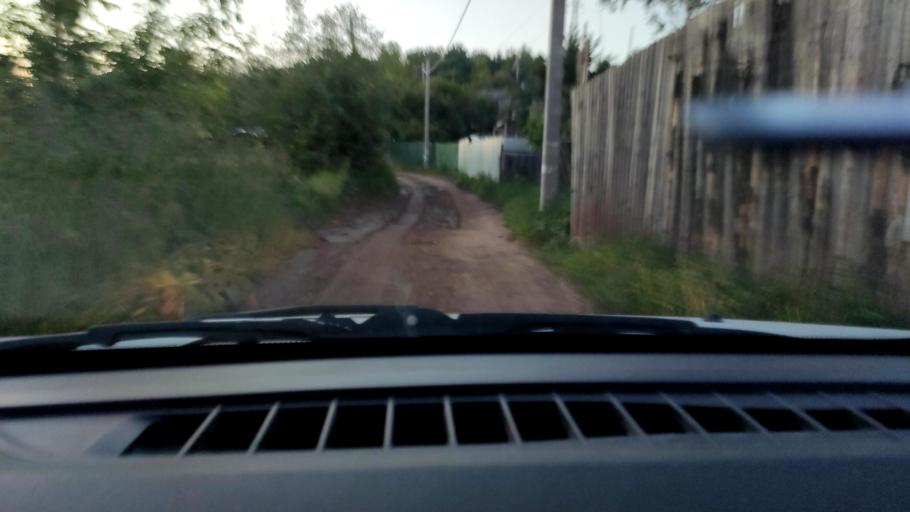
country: RU
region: Perm
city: Kondratovo
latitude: 57.9538
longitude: 56.1457
